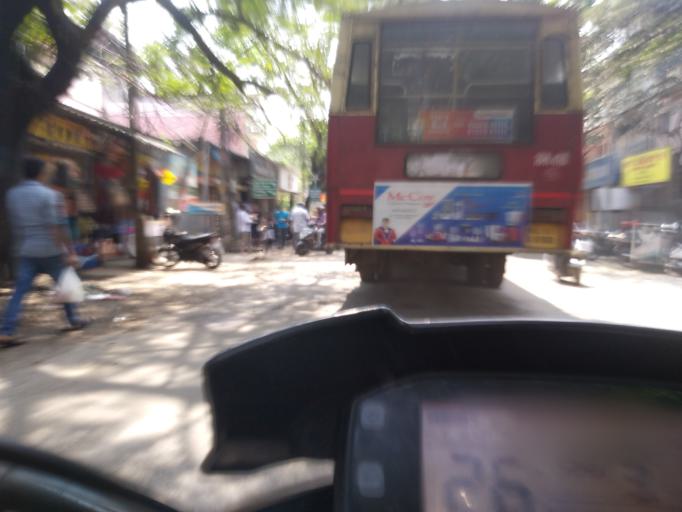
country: IN
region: Kerala
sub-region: Ernakulam
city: Cochin
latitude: 9.9771
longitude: 76.2932
